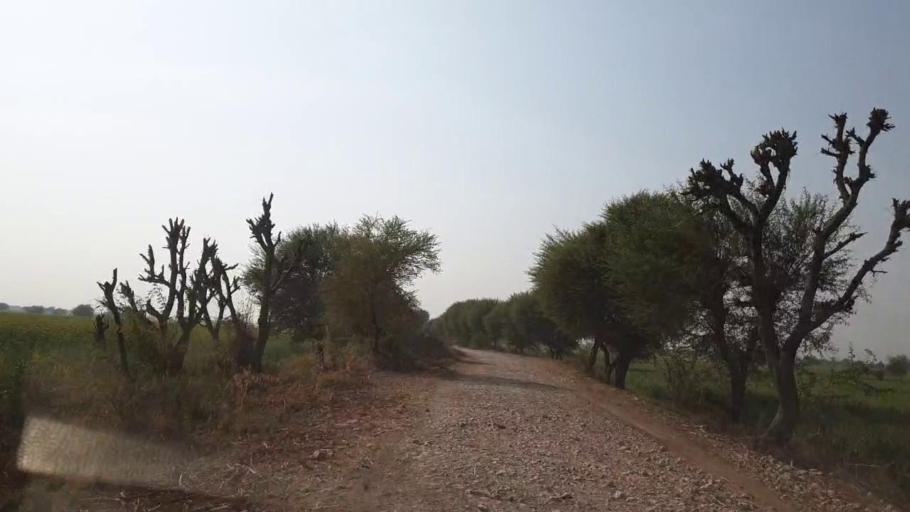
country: PK
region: Sindh
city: Pithoro
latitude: 25.6945
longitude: 69.2177
